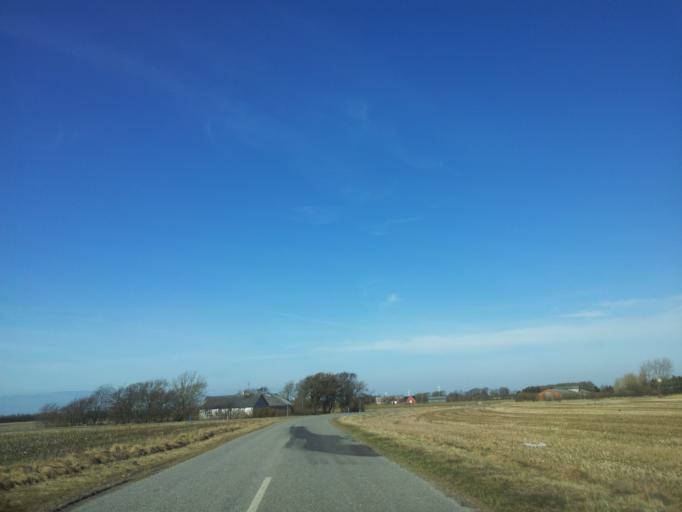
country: DK
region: South Denmark
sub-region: Tonder Kommune
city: Sherrebek
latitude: 55.1847
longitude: 8.7169
